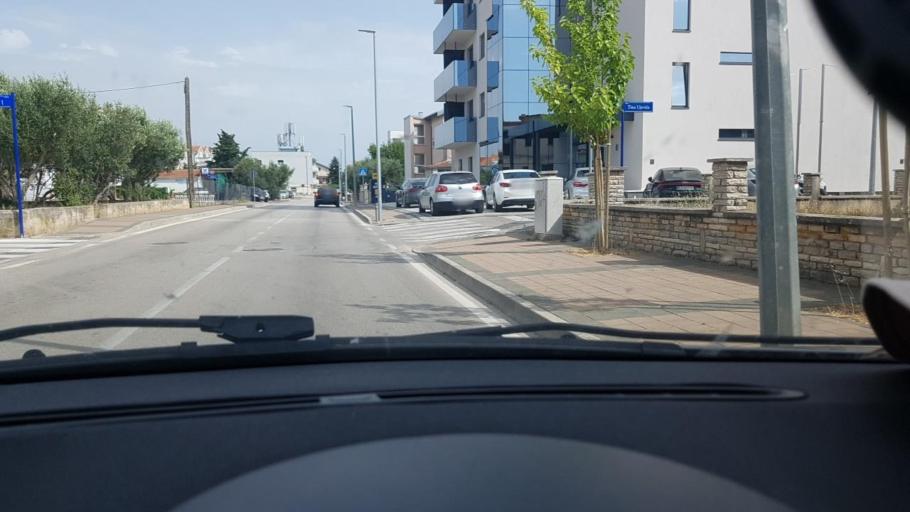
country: HR
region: Sibensko-Kniniska
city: Vodice
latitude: 43.7599
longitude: 15.7873
